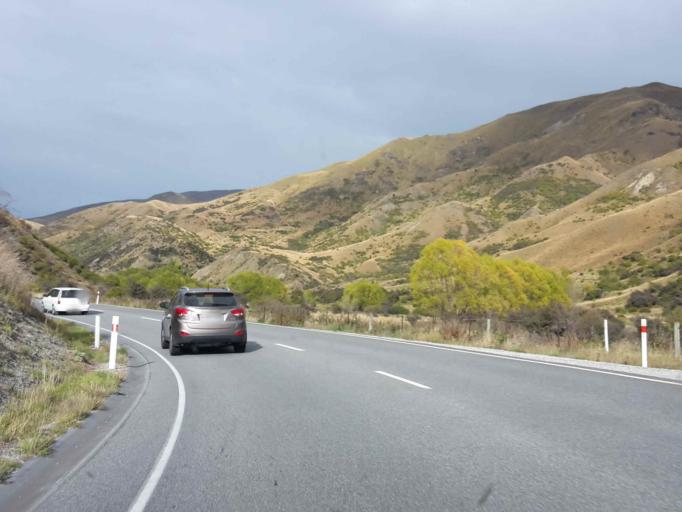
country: NZ
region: Otago
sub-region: Queenstown-Lakes District
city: Arrowtown
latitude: -44.9094
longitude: 168.9786
